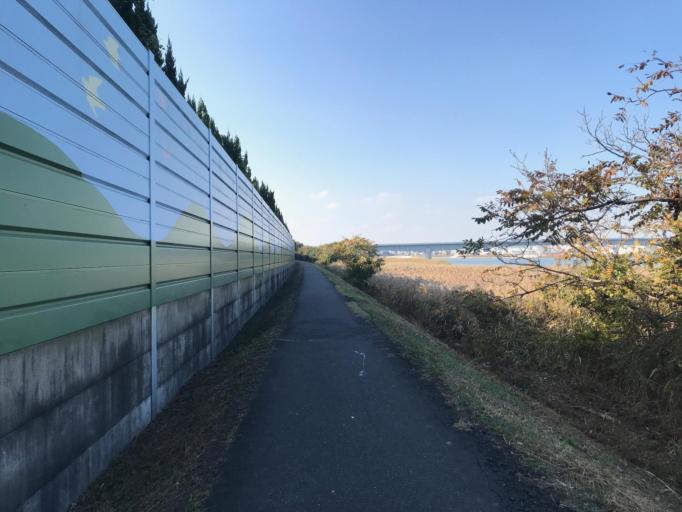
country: JP
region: Kanagawa
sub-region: Kawasaki-shi
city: Kawasaki
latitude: 35.5374
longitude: 139.7655
